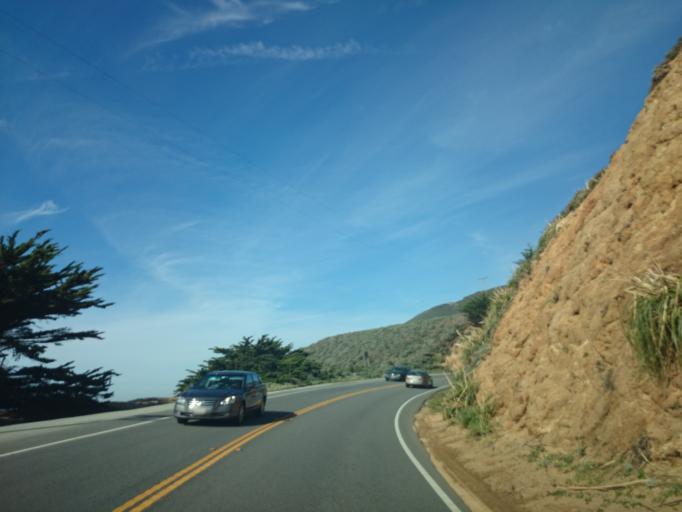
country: US
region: California
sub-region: San Mateo County
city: Montara
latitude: 37.5617
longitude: -122.5135
